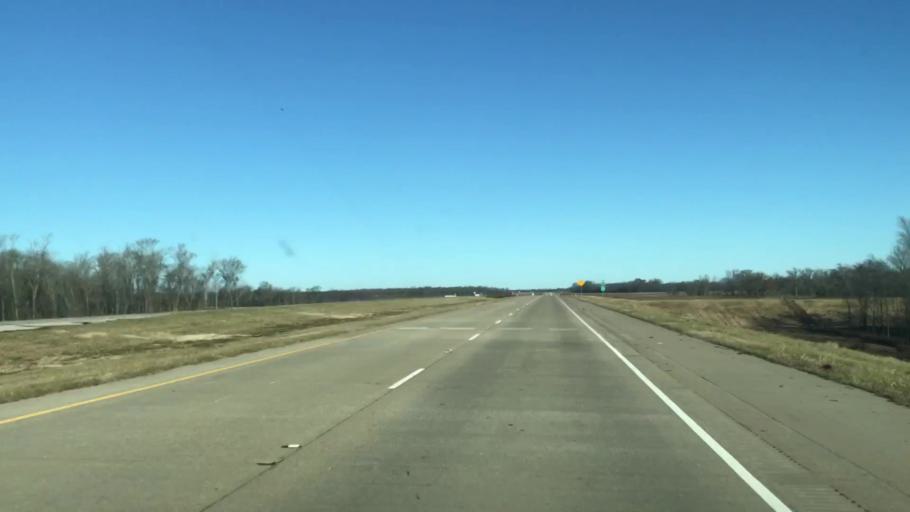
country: US
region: Louisiana
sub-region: Caddo Parish
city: Blanchard
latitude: 32.6276
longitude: -93.8367
